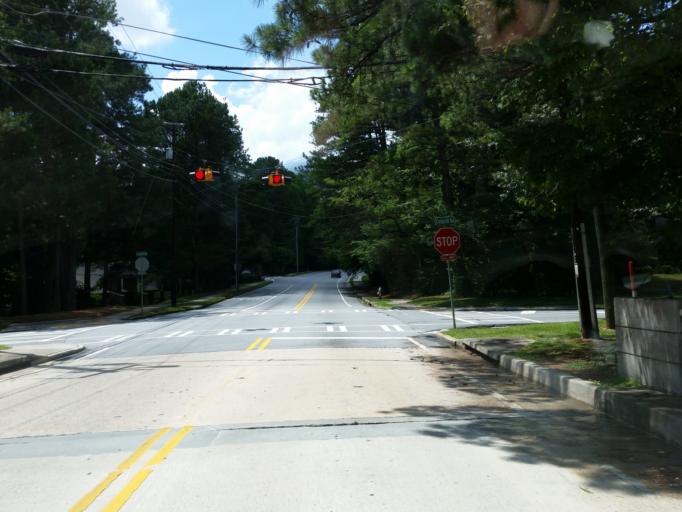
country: US
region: Georgia
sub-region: DeKalb County
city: Dunwoody
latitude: 33.9703
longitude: -84.3481
